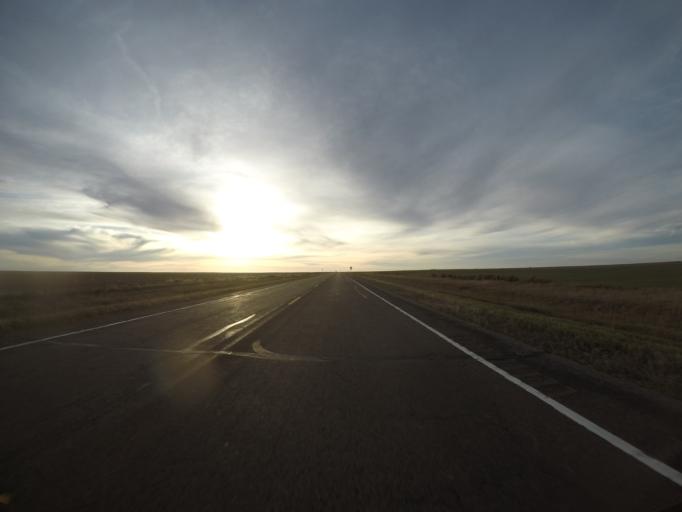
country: US
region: Colorado
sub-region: Washington County
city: Akron
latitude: 39.7274
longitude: -103.1533
